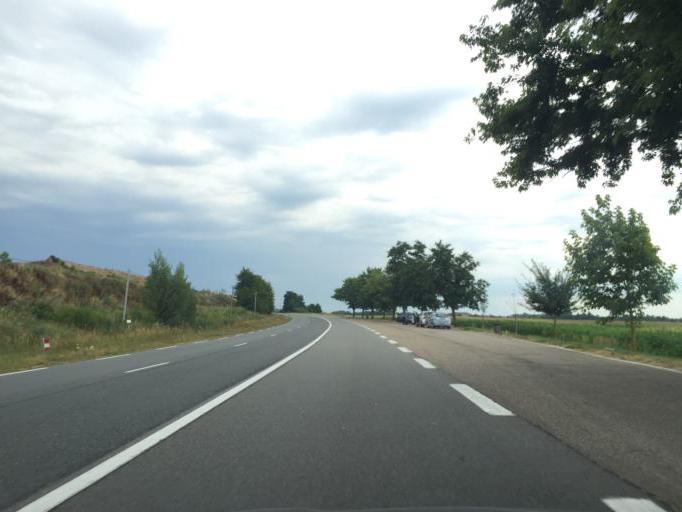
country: FR
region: Auvergne
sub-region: Departement de l'Allier
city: Varennes-sur-Allier
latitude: 46.3705
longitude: 3.3636
